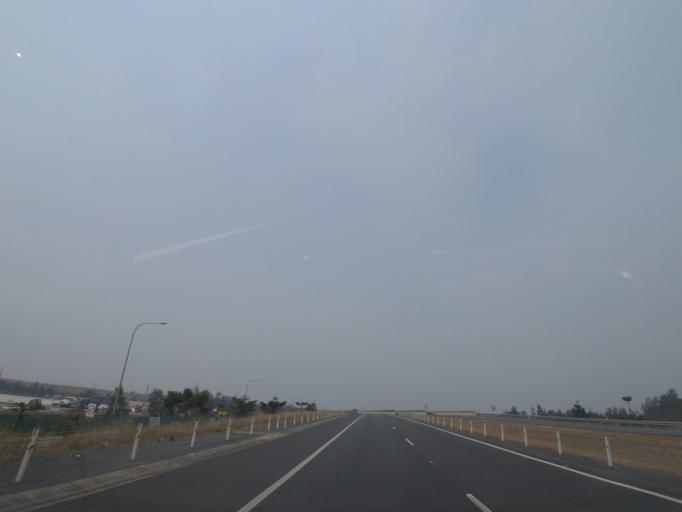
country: AU
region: New South Wales
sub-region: Ballina
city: Ballina
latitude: -28.8621
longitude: 153.5171
